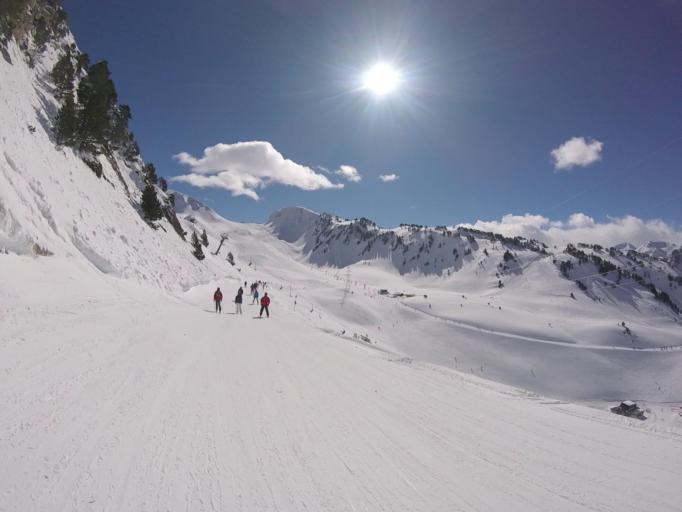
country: ES
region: Catalonia
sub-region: Provincia de Lleida
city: Espot
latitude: 42.6863
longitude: 0.9639
